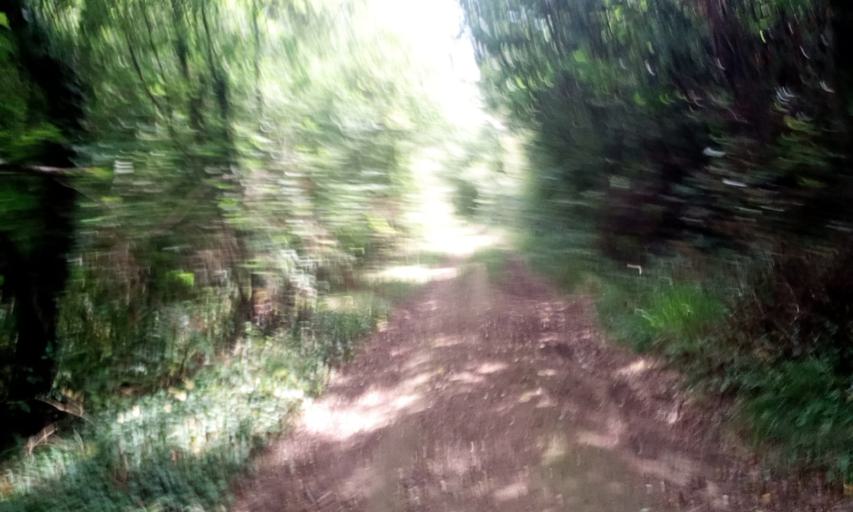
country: FR
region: Lower Normandy
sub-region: Departement du Calvados
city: Cagny
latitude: 49.1126
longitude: -0.2520
